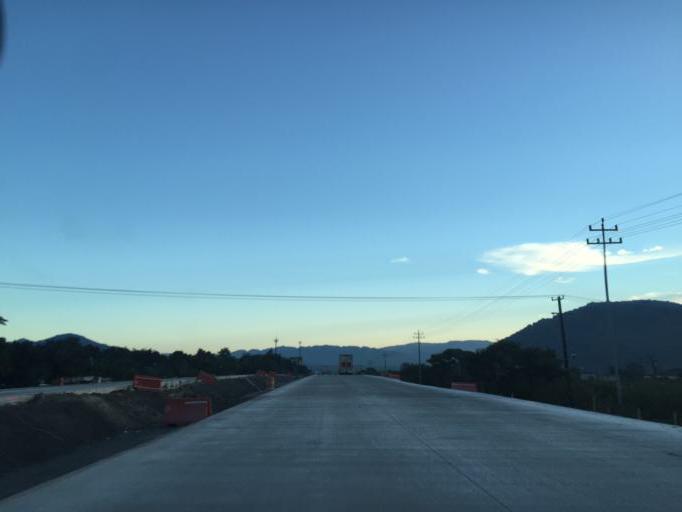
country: MX
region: Veracruz
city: Ixtac Zoquitlan
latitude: 18.8716
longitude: -97.0630
